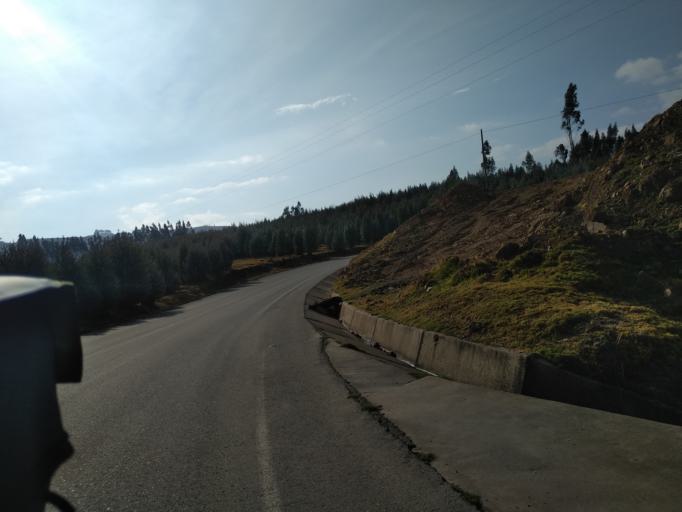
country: PE
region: La Libertad
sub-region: Provincia de Otuzco
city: Agallpampa
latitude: -7.9970
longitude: -78.5204
